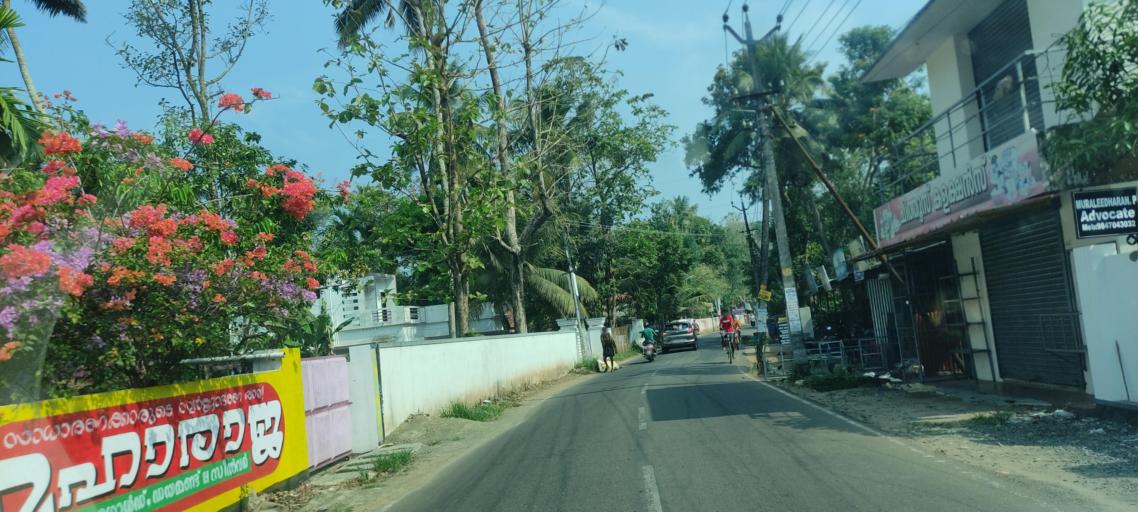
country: IN
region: Kerala
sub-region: Alappuzha
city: Kutiatodu
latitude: 9.7776
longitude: 76.3049
